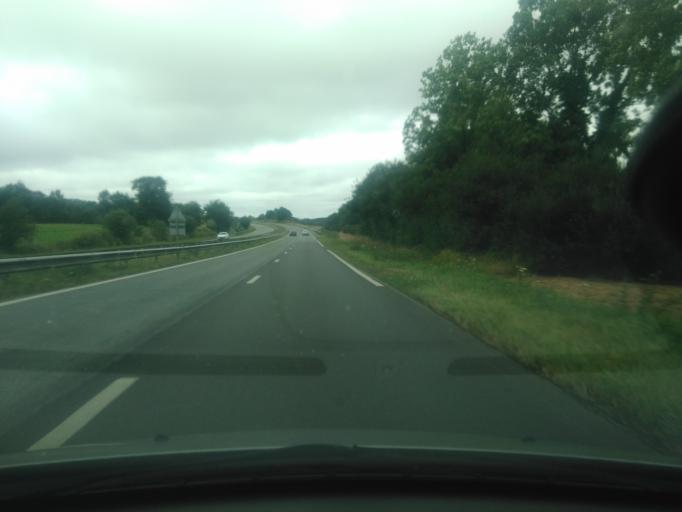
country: FR
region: Brittany
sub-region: Departement des Cotes-d'Armor
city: Jugon-les-Lacs
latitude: 48.4105
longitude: -2.3537
